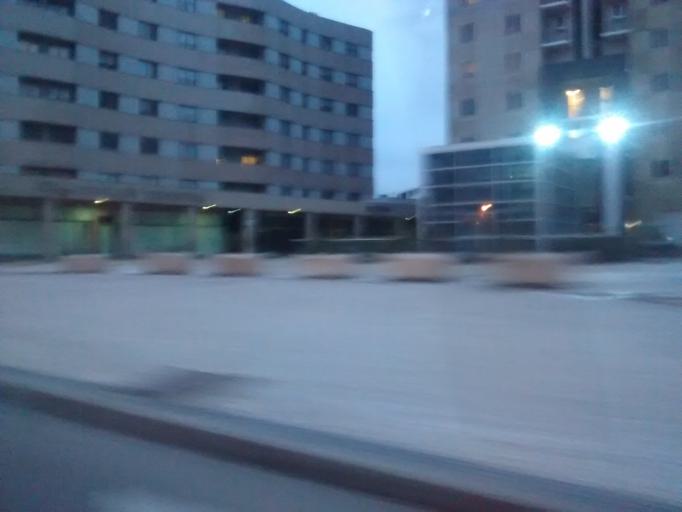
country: PT
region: Aveiro
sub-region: Aveiro
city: Aveiro
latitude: 40.6420
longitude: -8.6464
